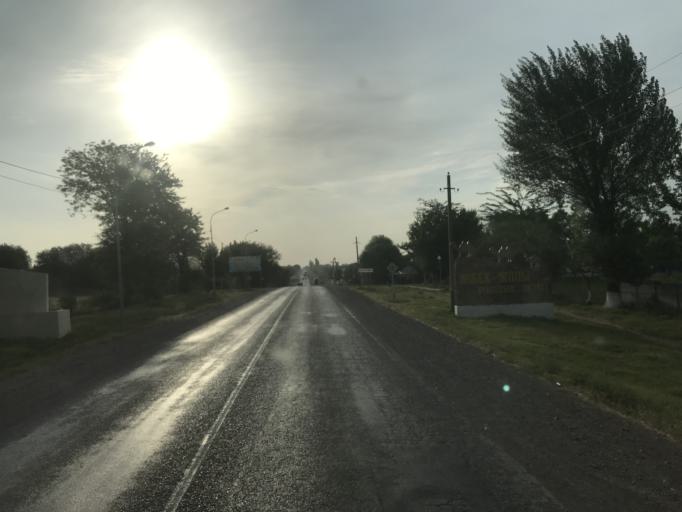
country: KZ
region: Ongtustik Qazaqstan
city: Saryaghash
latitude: 41.4936
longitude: 69.3025
